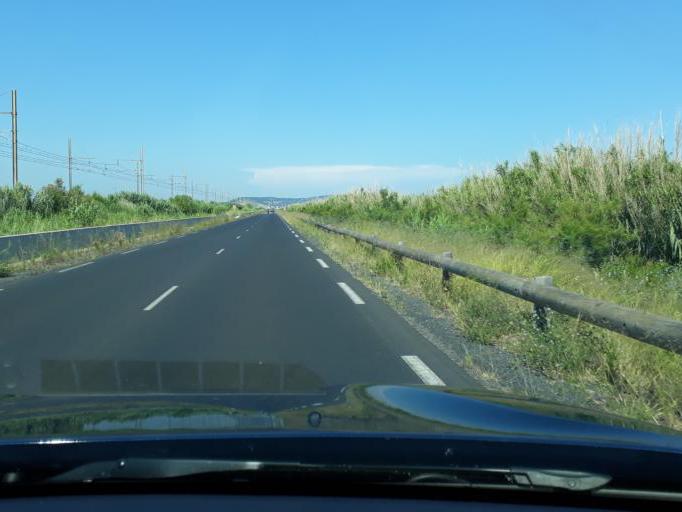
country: FR
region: Languedoc-Roussillon
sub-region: Departement de l'Herault
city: Meze
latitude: 43.3589
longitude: 3.6016
